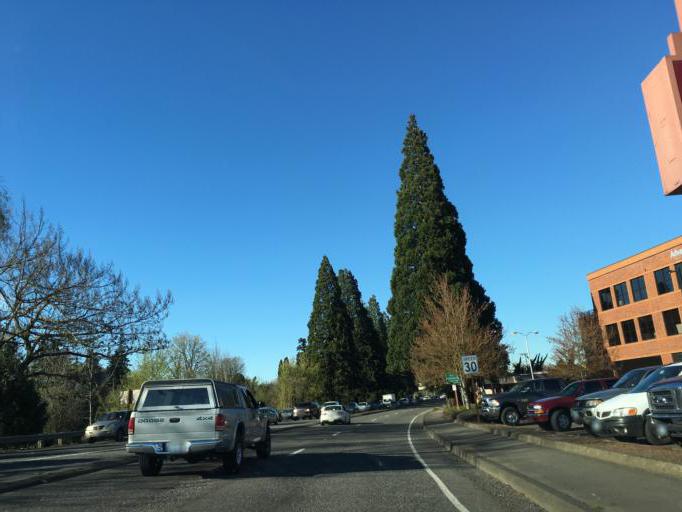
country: US
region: Oregon
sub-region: Clackamas County
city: Milwaukie
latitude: 45.4462
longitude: -122.6428
